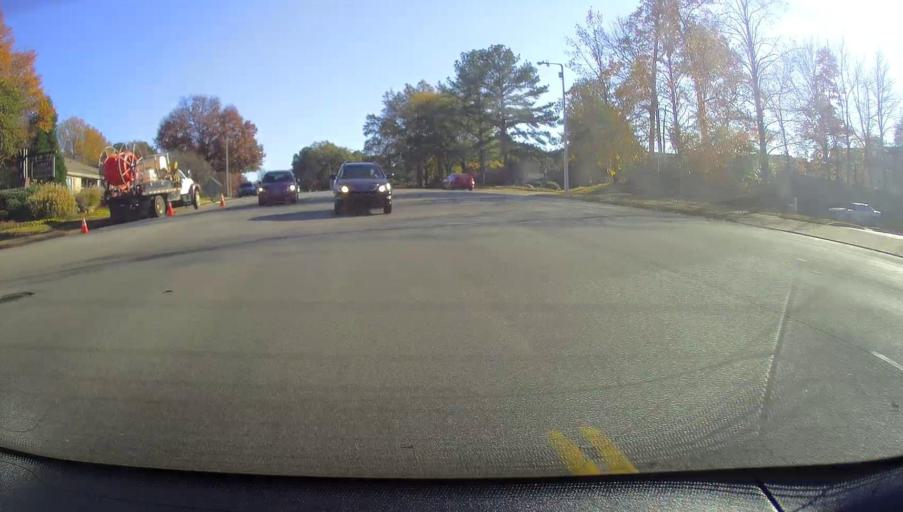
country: US
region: Tennessee
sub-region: Shelby County
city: Germantown
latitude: 35.1042
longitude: -89.8418
